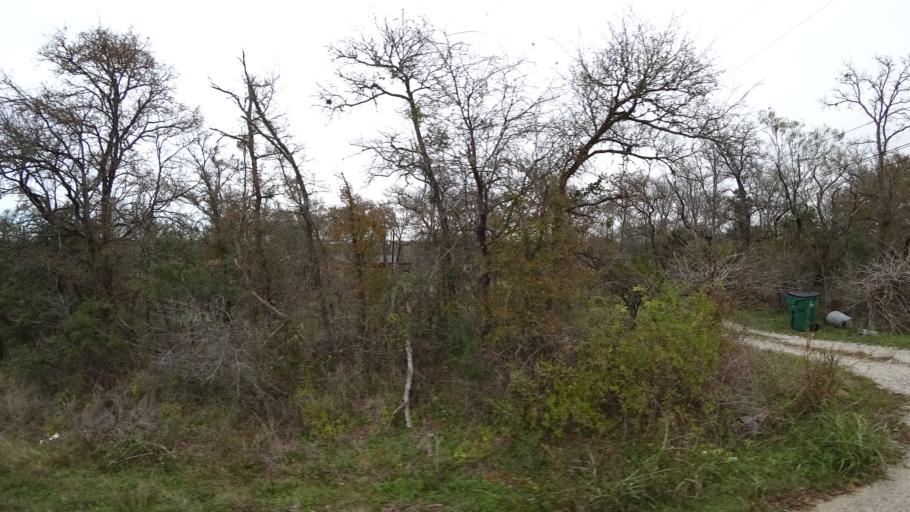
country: US
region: Texas
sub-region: Travis County
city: Garfield
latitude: 30.0979
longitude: -97.5736
